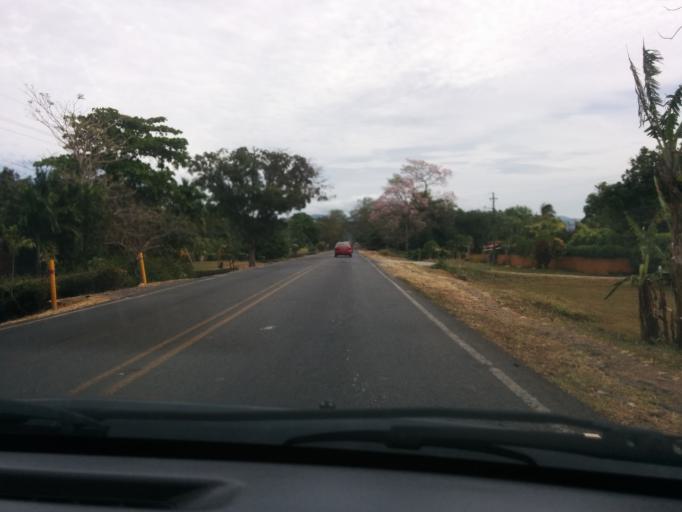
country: CR
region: Puntarenas
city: Esparza
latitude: 10.0012
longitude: -84.6438
